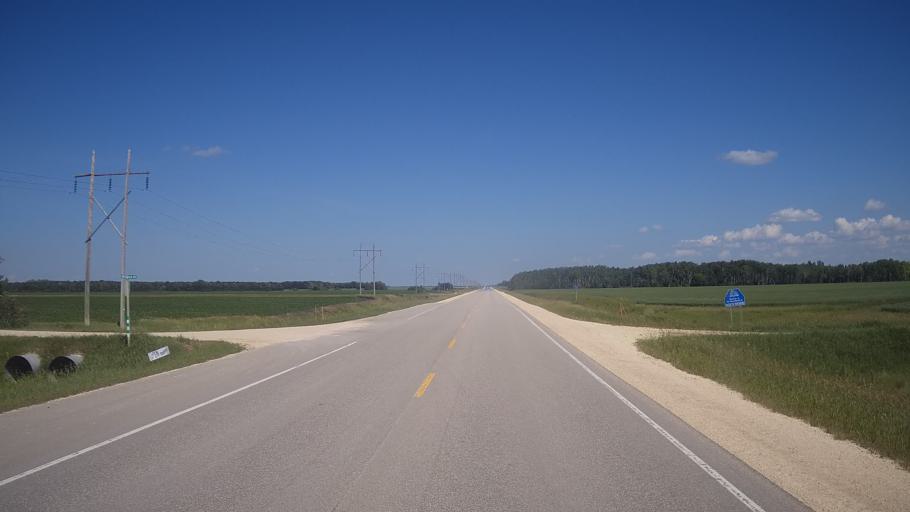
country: CA
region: Manitoba
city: Stonewall
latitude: 50.1227
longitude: -97.4601
